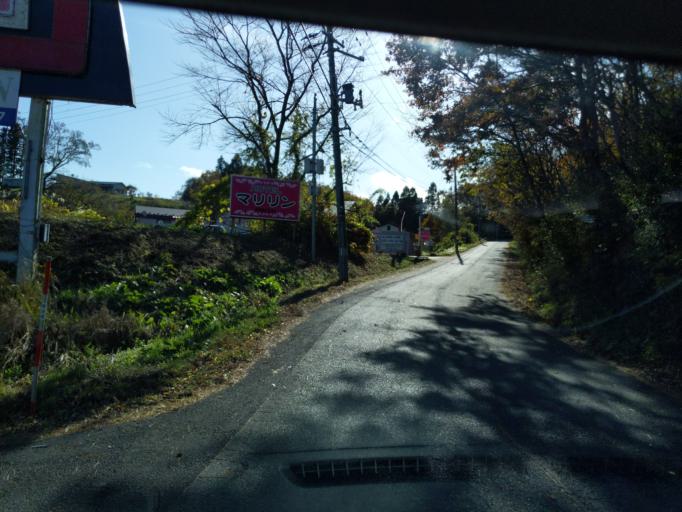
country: JP
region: Iwate
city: Mizusawa
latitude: 39.0912
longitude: 141.1200
